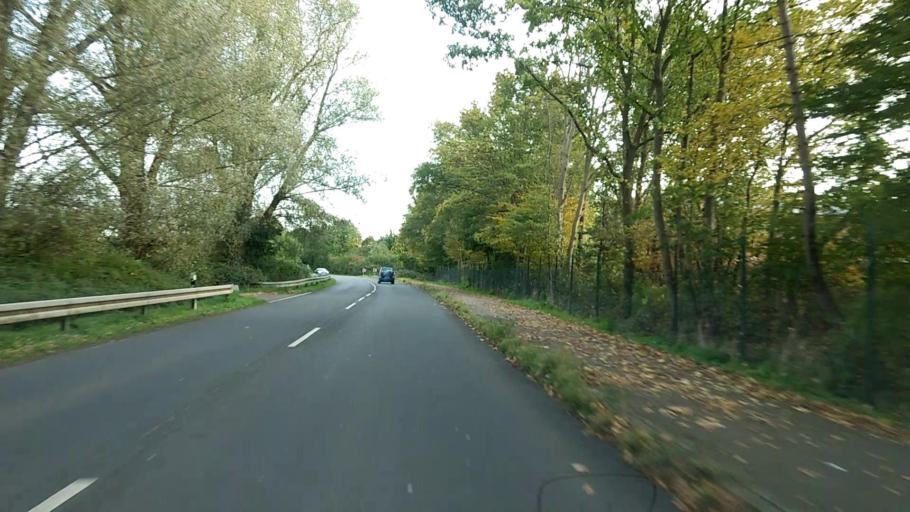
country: DE
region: North Rhine-Westphalia
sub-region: Regierungsbezirk Koln
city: Bergheim
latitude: 50.9400
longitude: 6.6579
